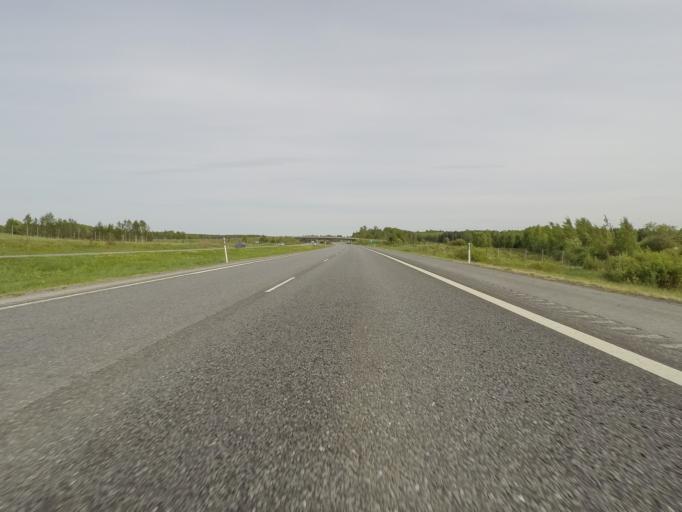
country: FI
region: Pirkanmaa
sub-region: Etelae-Pirkanmaa
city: Akaa
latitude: 61.1666
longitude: 23.9452
